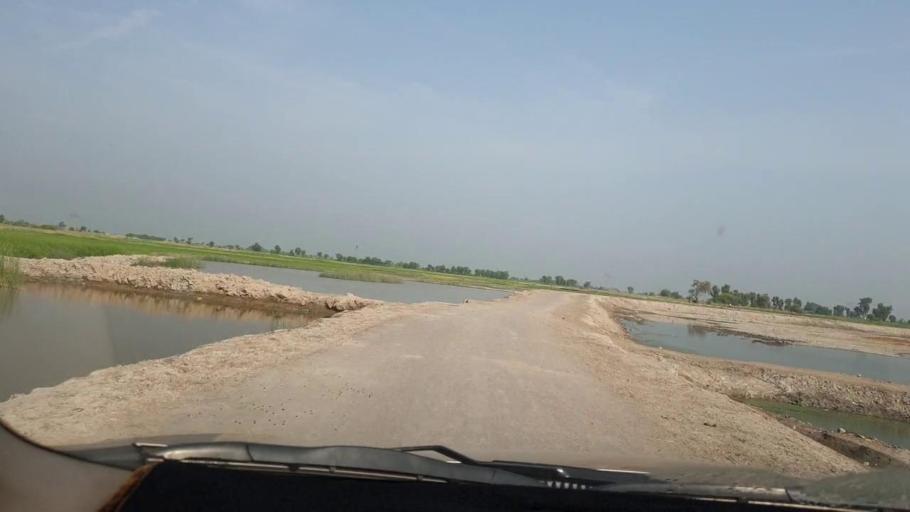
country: PK
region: Sindh
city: Goth Garelo
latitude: 27.4663
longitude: 68.0815
